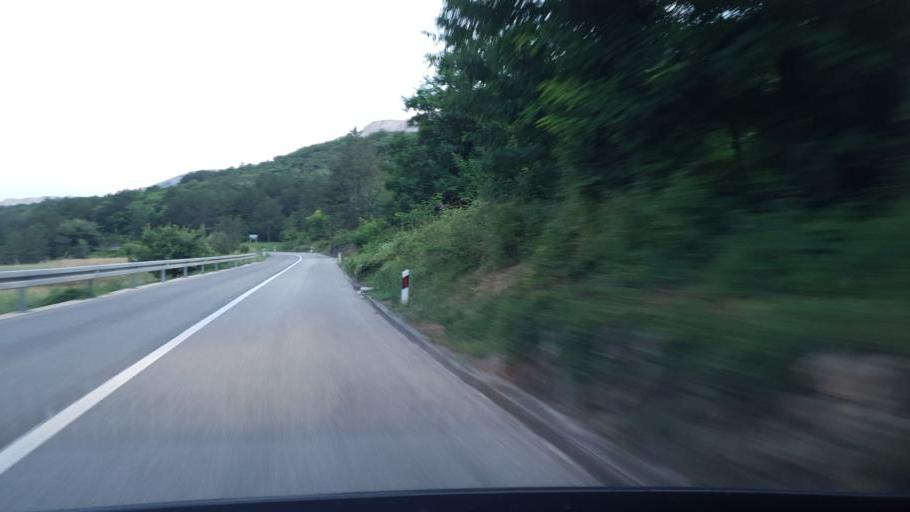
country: HR
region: Primorsko-Goranska
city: Punat
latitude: 45.0076
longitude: 14.7024
